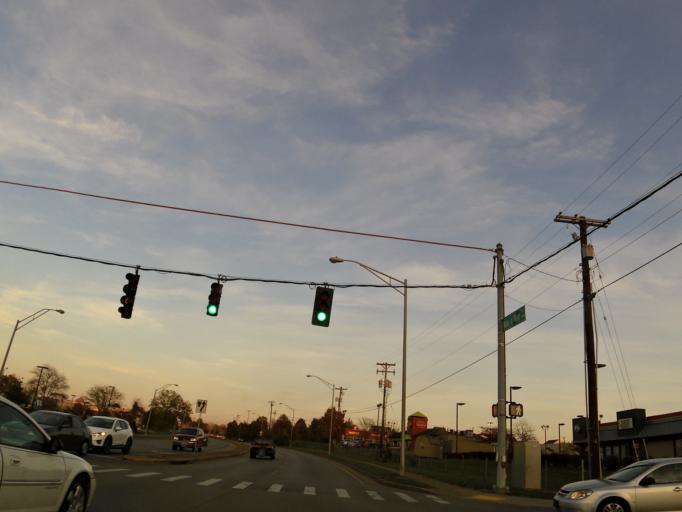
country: US
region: Kentucky
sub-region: Fayette County
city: Lexington
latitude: 37.9680
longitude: -84.5026
